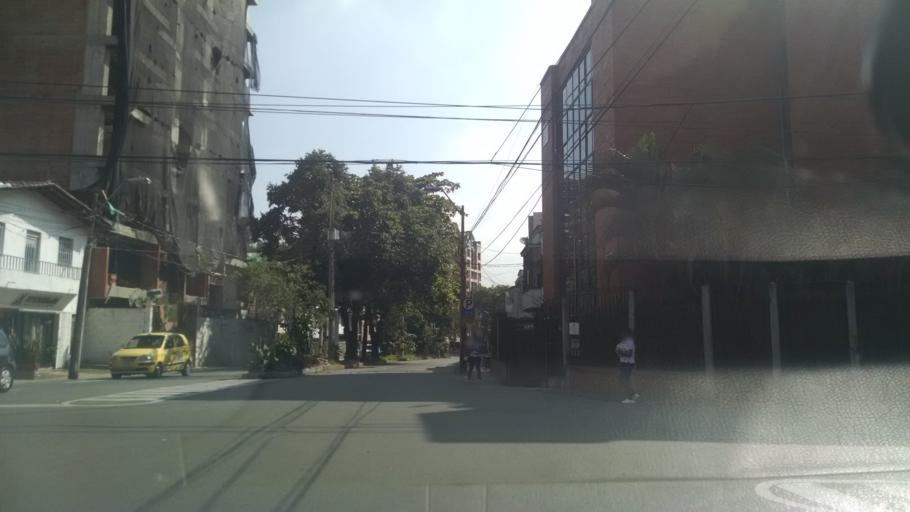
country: CO
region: Antioquia
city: Medellin
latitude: 6.2461
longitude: -75.5914
